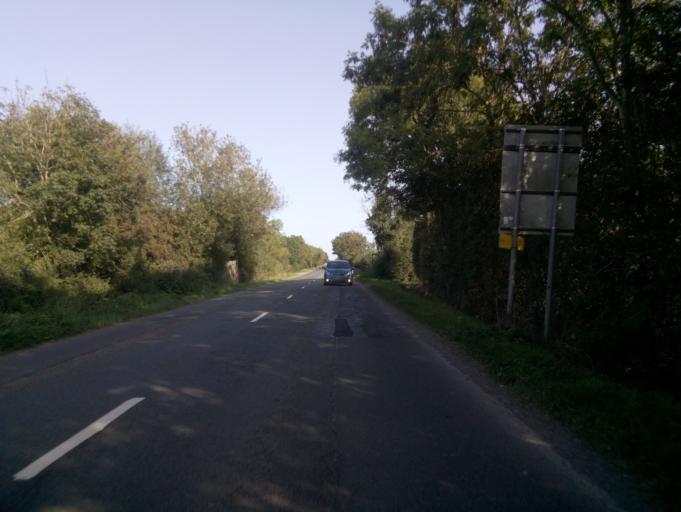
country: GB
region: England
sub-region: Gloucestershire
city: Gloucester
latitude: 51.9623
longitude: -2.2711
